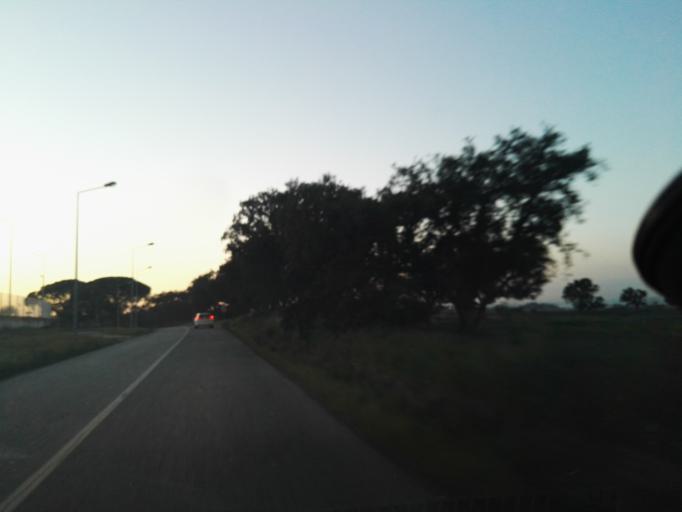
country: PT
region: Setubal
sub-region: Alcochete
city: Alcochete
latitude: 38.7277
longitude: -8.9115
